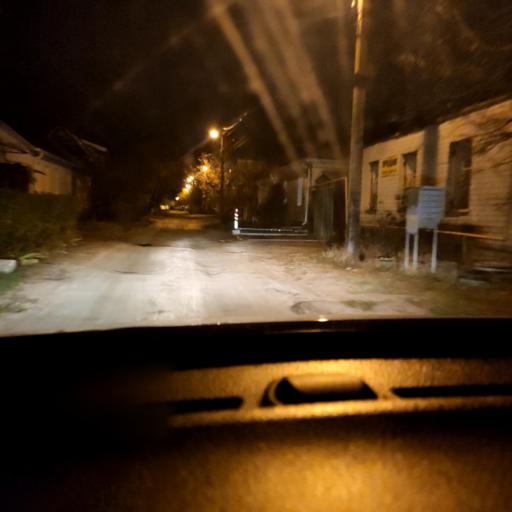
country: RU
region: Voronezj
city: Somovo
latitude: 51.7408
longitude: 39.2734
